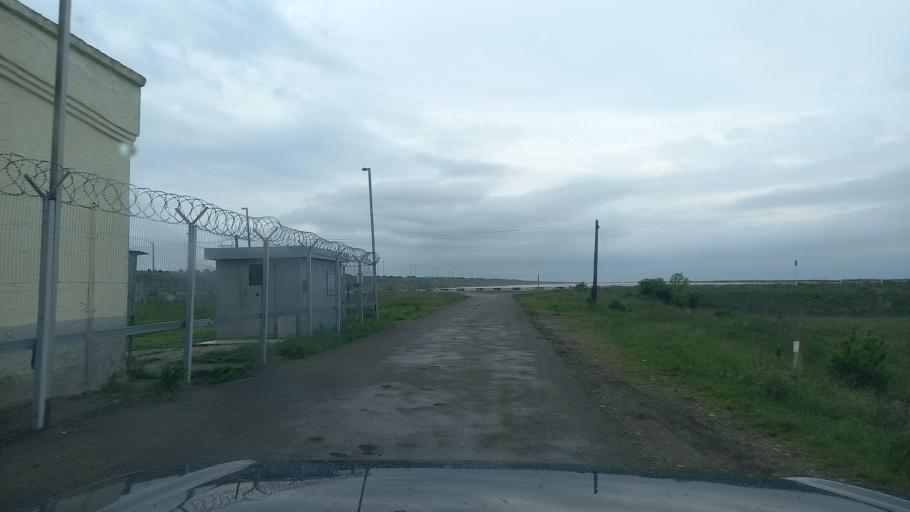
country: RU
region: Stavropol'skiy
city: Nevinnomyssk
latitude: 44.5911
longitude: 42.2314
